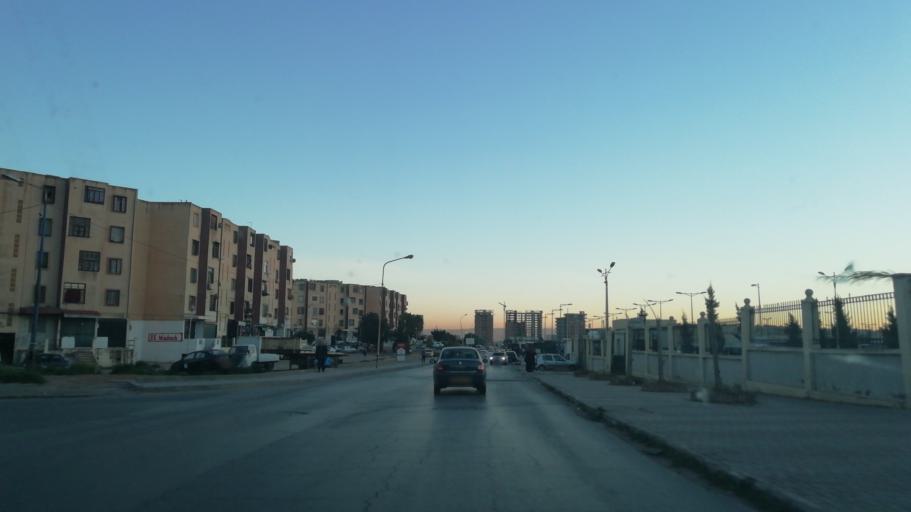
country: DZ
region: Oran
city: Bir el Djir
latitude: 35.7060
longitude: -0.5909
